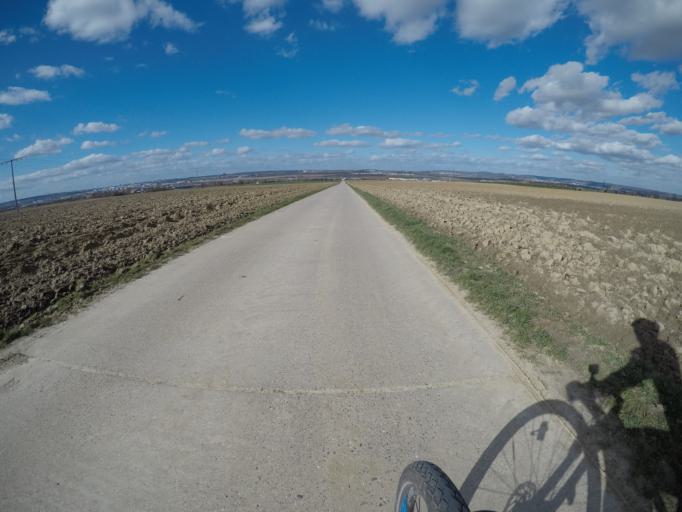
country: DE
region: Baden-Wuerttemberg
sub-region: Regierungsbezirk Stuttgart
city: Filderstadt
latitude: 48.6588
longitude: 9.2489
